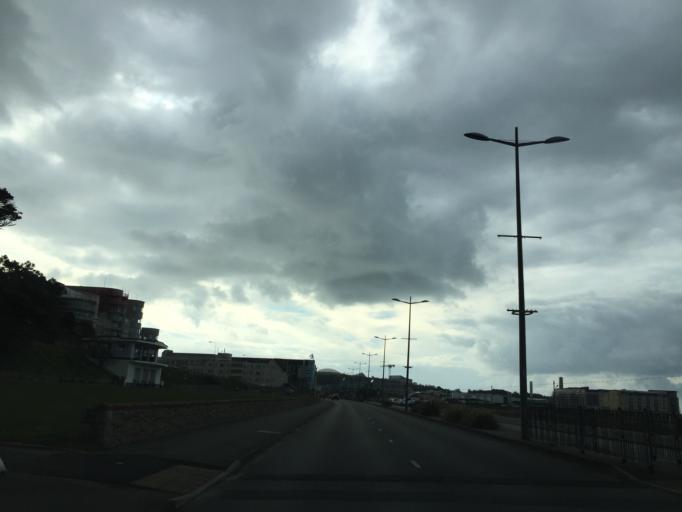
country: JE
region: St Helier
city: Saint Helier
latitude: 49.1894
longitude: -2.1198
